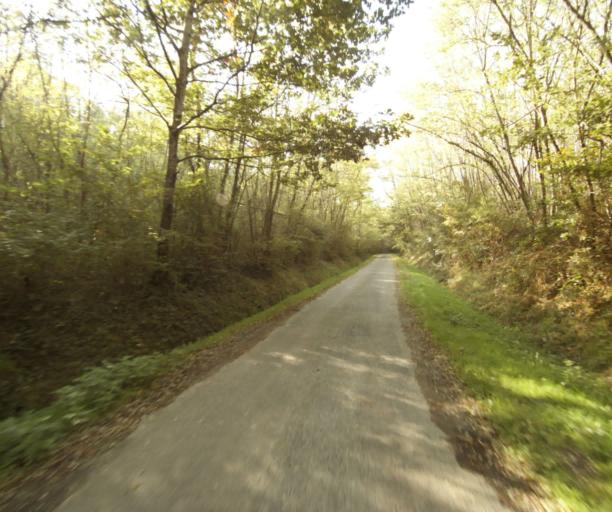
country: FR
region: Midi-Pyrenees
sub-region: Departement du Tarn-et-Garonne
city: Nohic
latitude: 43.9254
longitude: 1.4457
